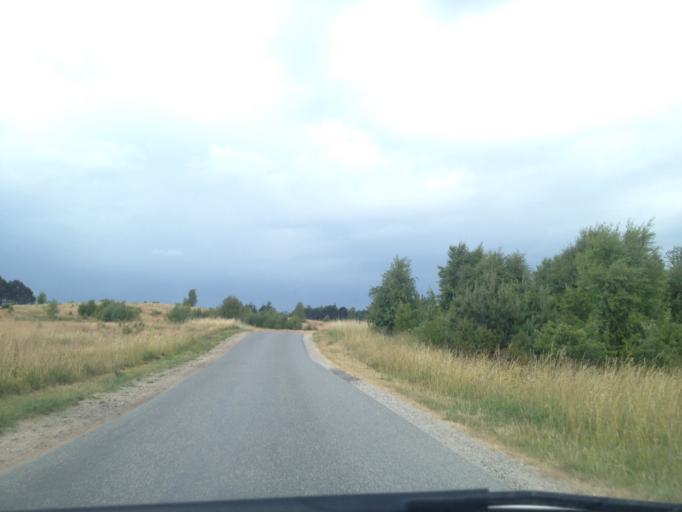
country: DK
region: Central Jutland
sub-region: Syddjurs Kommune
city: Ebeltoft
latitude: 56.1631
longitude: 10.6852
